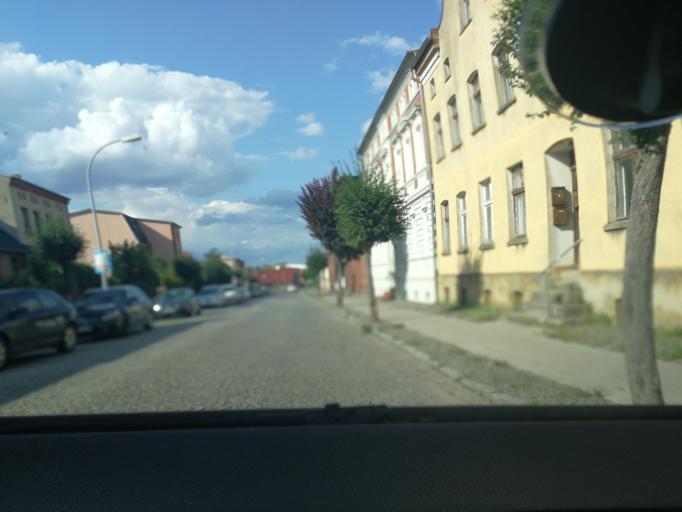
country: DE
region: Brandenburg
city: Pritzwalk
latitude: 53.1489
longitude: 12.1845
